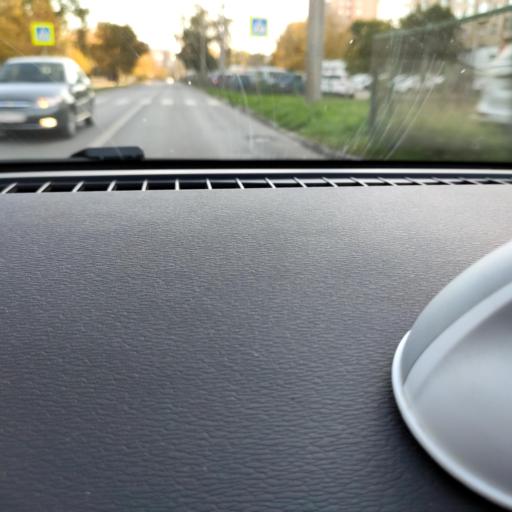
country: RU
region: Samara
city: Samara
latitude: 53.1943
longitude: 50.2001
